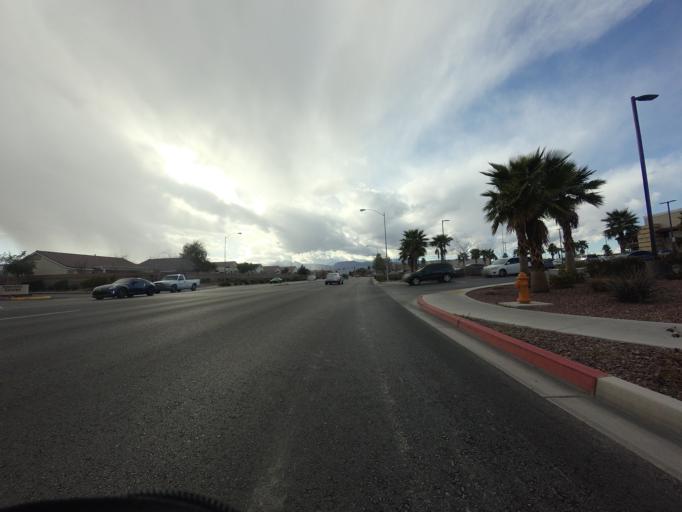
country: US
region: Nevada
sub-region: Clark County
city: North Las Vegas
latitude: 36.2691
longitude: -115.2044
